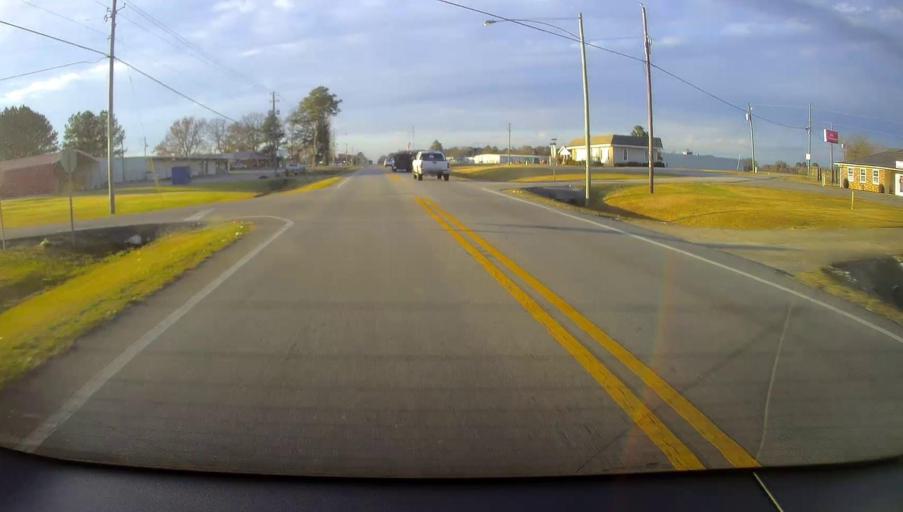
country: US
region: Alabama
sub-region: Blount County
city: Oneonta
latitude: 34.1157
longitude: -86.3890
